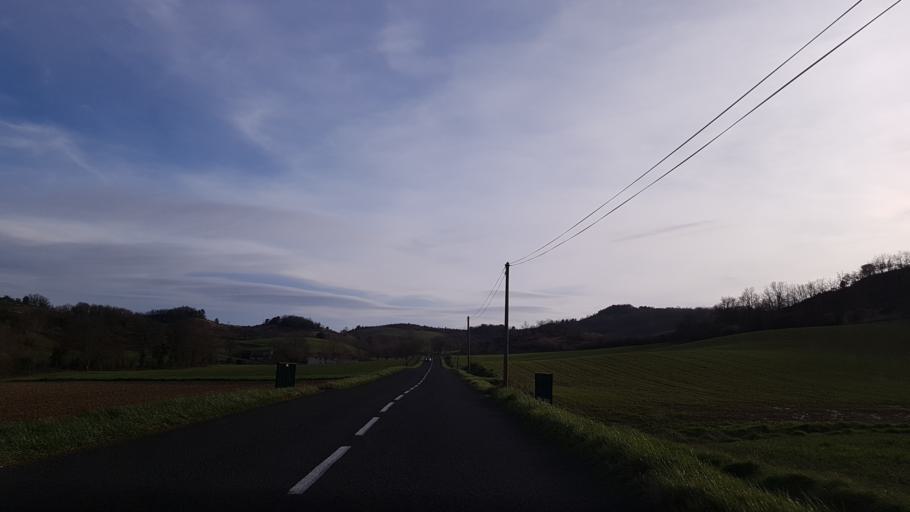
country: FR
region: Midi-Pyrenees
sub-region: Departement de l'Ariege
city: Mirepoix
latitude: 43.1415
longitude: 1.9125
